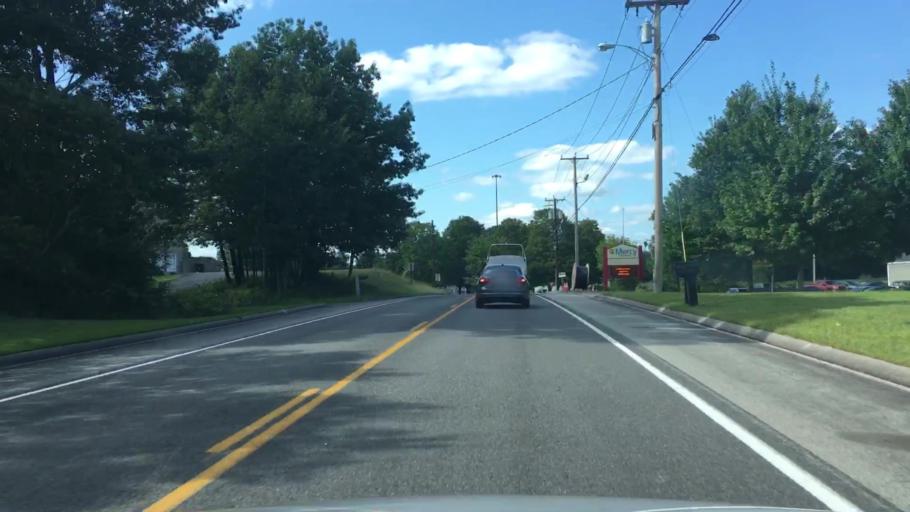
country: US
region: Maine
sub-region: Cumberland County
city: North Windham
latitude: 43.8012
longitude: -70.4044
